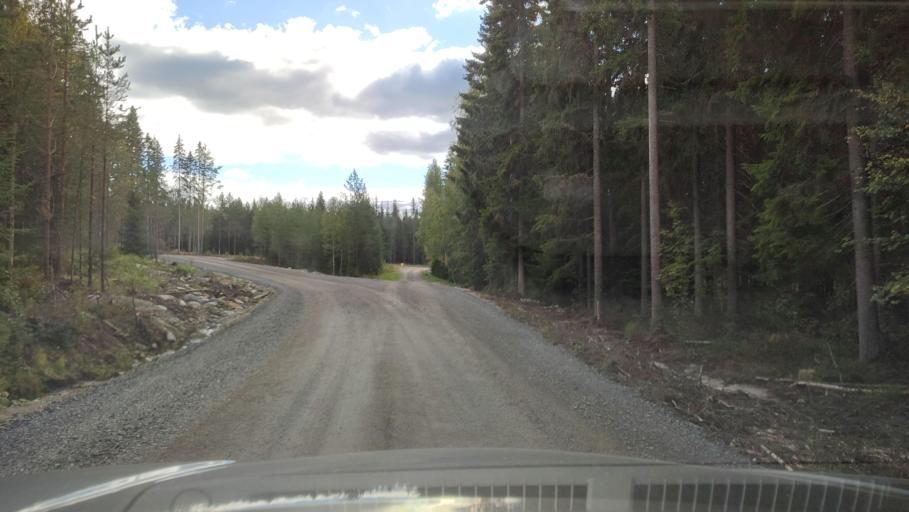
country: FI
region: Southern Ostrobothnia
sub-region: Suupohja
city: Karijoki
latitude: 62.2054
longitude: 21.5995
